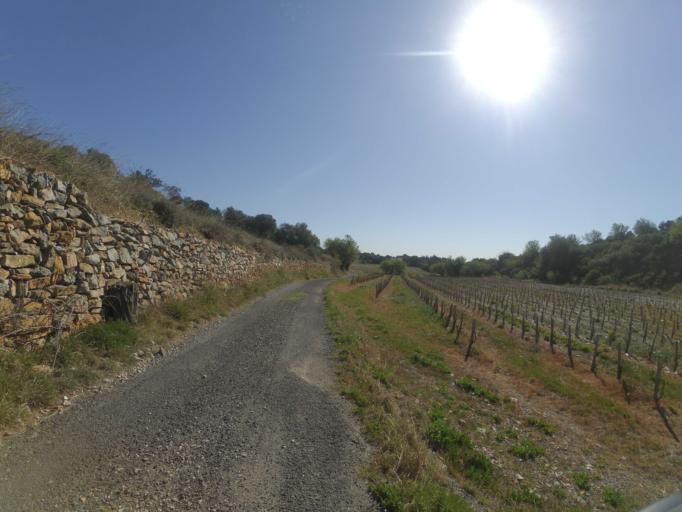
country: FR
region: Languedoc-Roussillon
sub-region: Departement des Pyrenees-Orientales
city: Baixas
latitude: 42.7606
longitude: 2.7701
